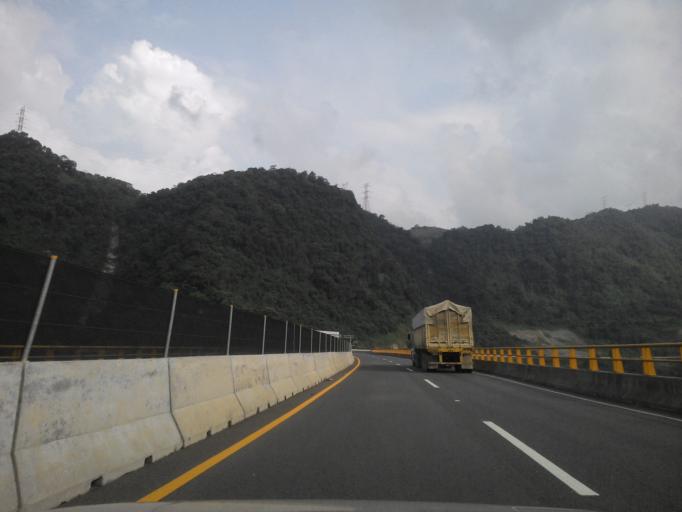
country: MX
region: Puebla
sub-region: Xicotepec
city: San Lorenzo
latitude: 20.3401
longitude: -97.9607
